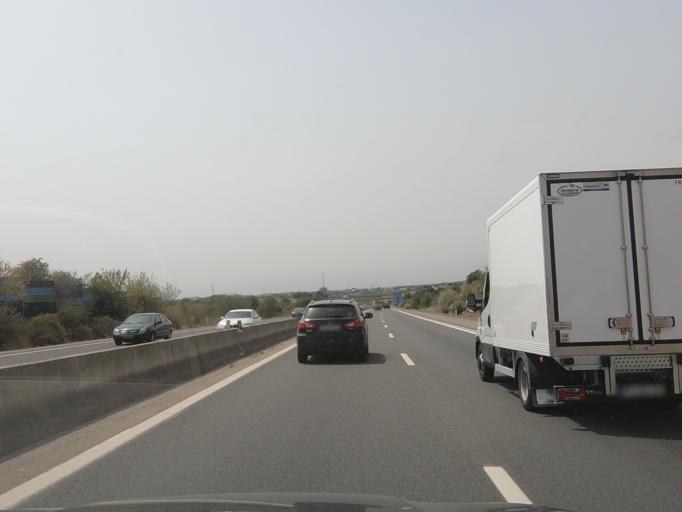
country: PT
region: Faro
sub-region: Albufeira
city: Guia
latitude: 37.1372
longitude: -8.3013
